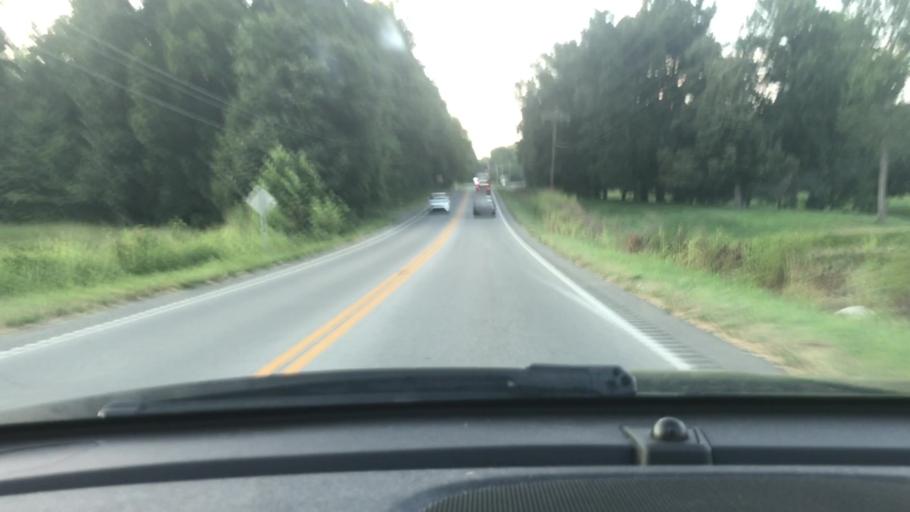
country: US
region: Tennessee
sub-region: Dickson County
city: Dickson
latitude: 36.0968
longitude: -87.3754
